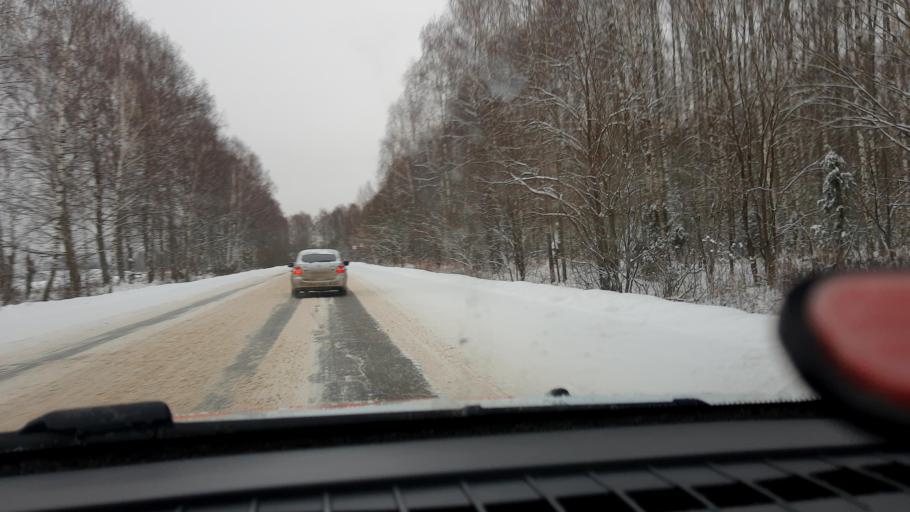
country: RU
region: Nizjnij Novgorod
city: Pamyat' Parizhskoy Kommuny
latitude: 56.2527
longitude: 44.4732
